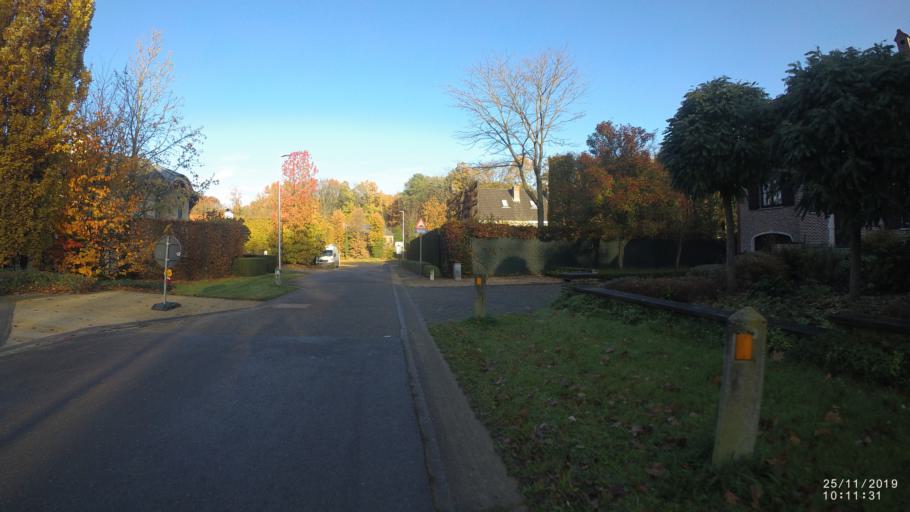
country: BE
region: Flanders
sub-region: Provincie Vlaams-Brabant
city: Diest
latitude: 50.9963
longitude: 5.0245
